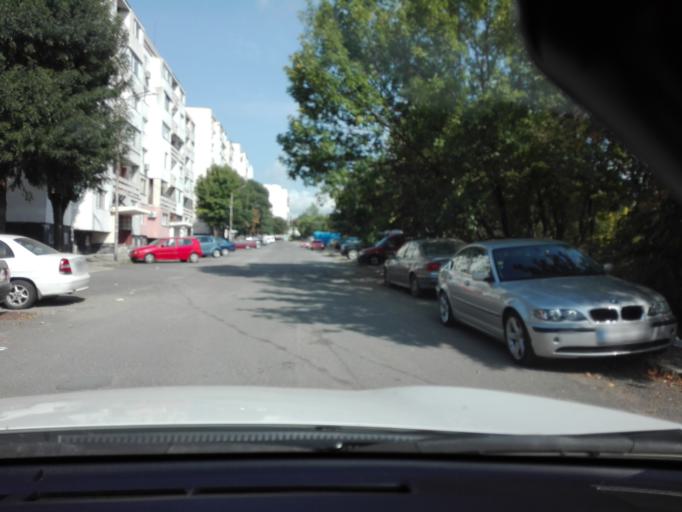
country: BG
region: Burgas
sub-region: Obshtina Burgas
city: Burgas
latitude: 42.4526
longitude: 27.4248
